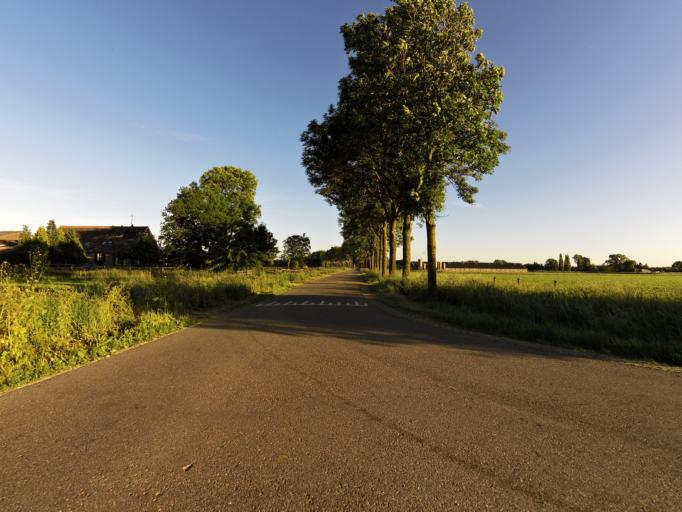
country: NL
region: Gelderland
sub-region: Gemeente Zevenaar
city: Zevenaar
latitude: 51.9524
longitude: 6.0757
